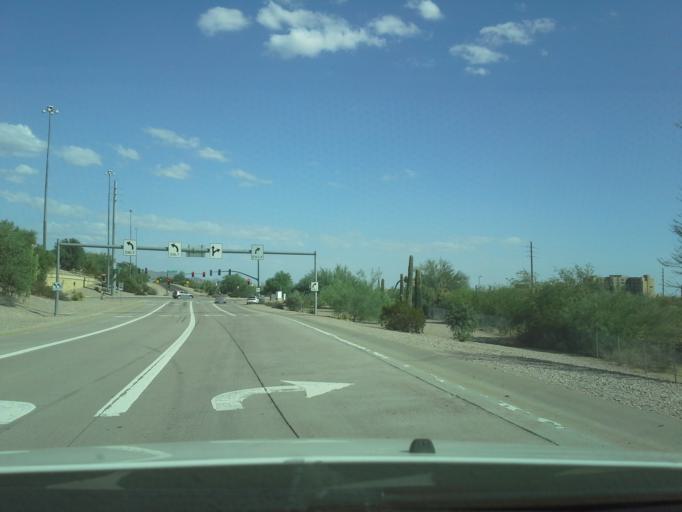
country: US
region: Arizona
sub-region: Maricopa County
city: Paradise Valley
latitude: 33.6680
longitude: -111.9616
